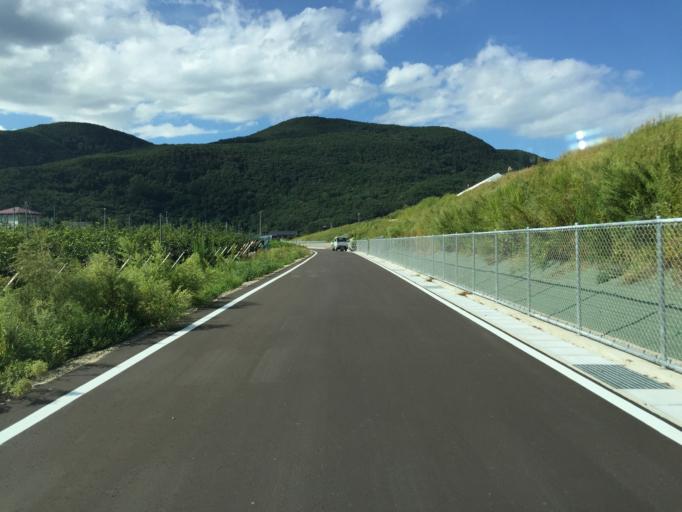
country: JP
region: Fukushima
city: Fukushima-shi
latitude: 37.8017
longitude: 140.4101
